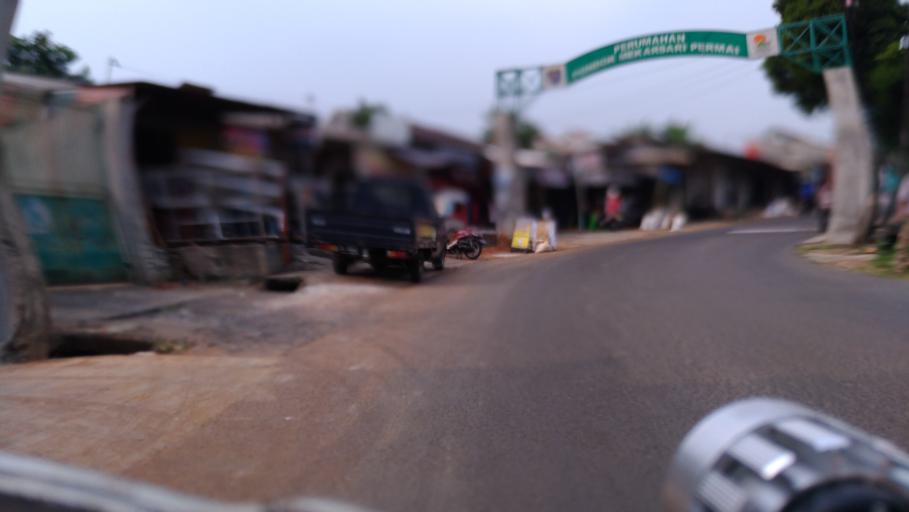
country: ID
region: West Java
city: Depok
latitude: -6.3655
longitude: 106.8618
